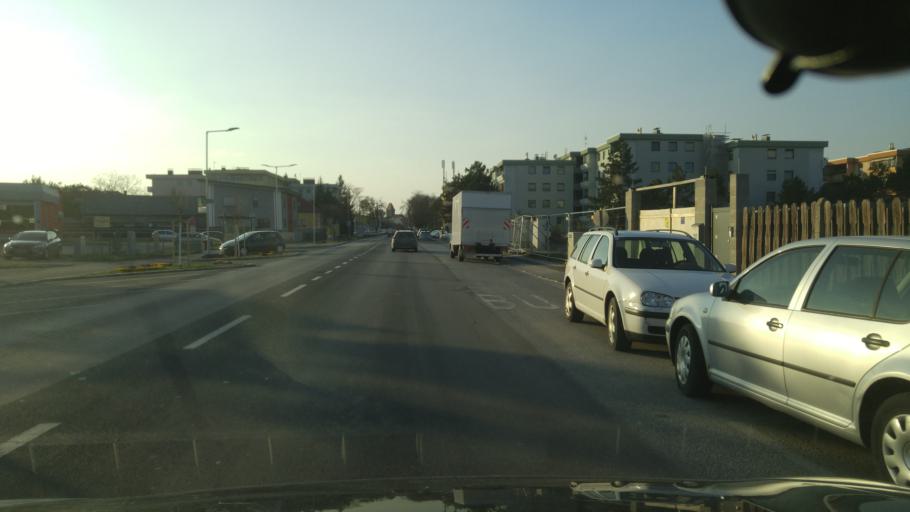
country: AT
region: Lower Austria
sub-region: Politischer Bezirk Wien-Umgebung
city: Himberg
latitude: 48.0768
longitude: 16.4454
